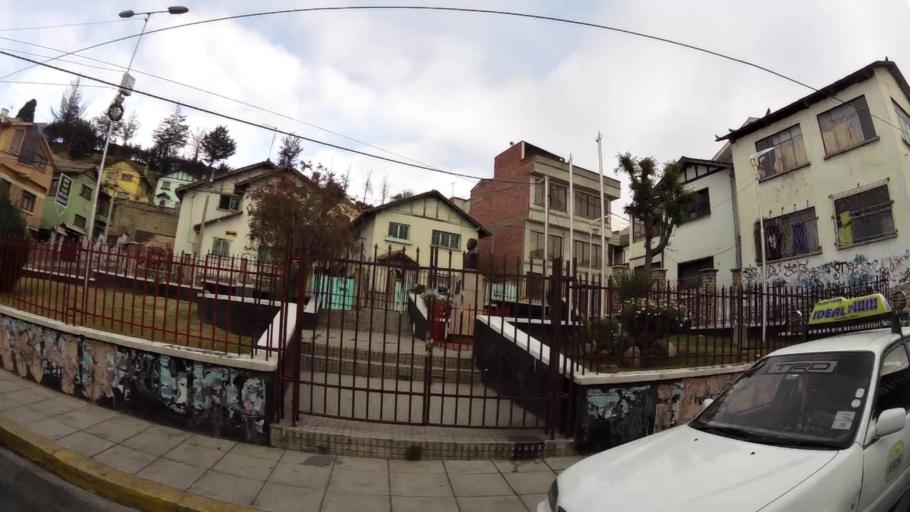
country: BO
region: La Paz
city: La Paz
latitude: -16.5027
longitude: -68.1234
